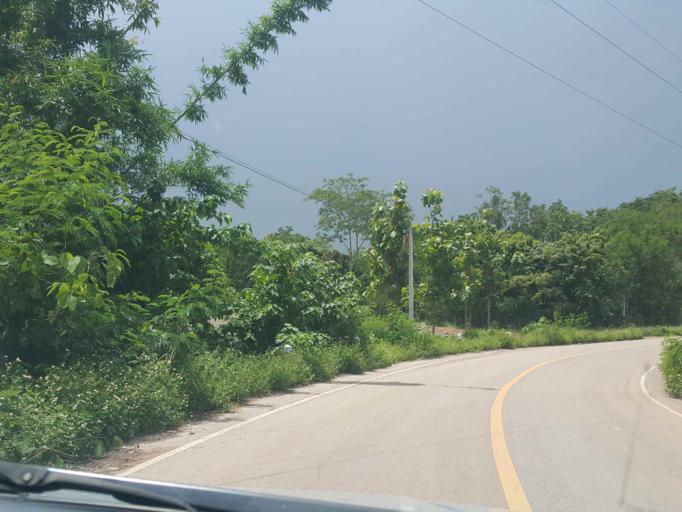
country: TH
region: Phayao
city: Dok Kham Tai
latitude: 19.0501
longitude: 99.9505
